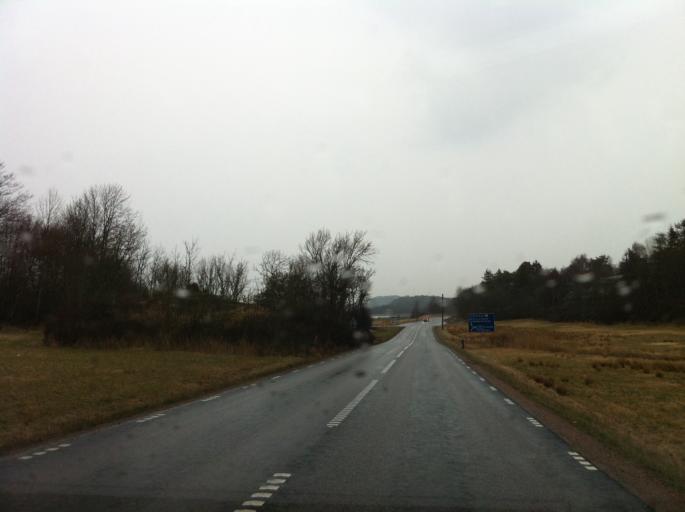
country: SE
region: Vaestra Goetaland
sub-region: Sotenas Kommun
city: Kungshamn
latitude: 58.3922
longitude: 11.2631
